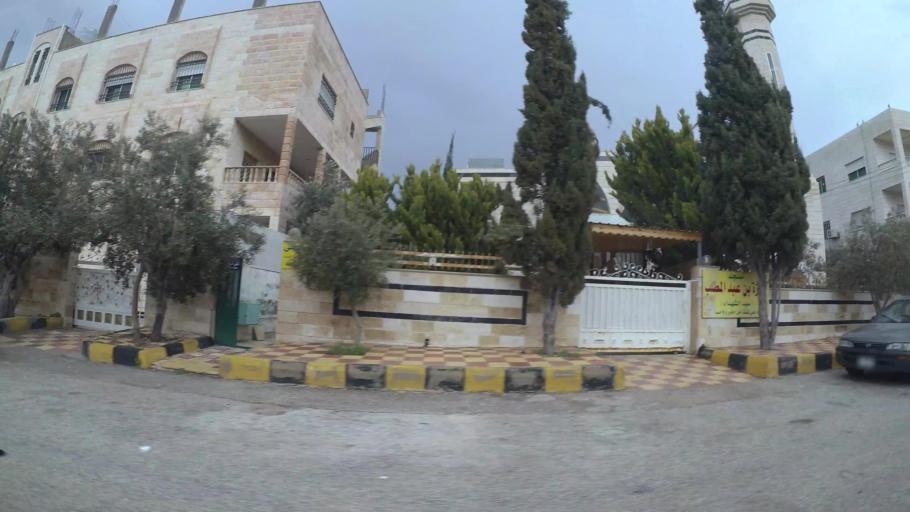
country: JO
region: Amman
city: Al Jubayhah
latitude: 32.0437
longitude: 35.8381
